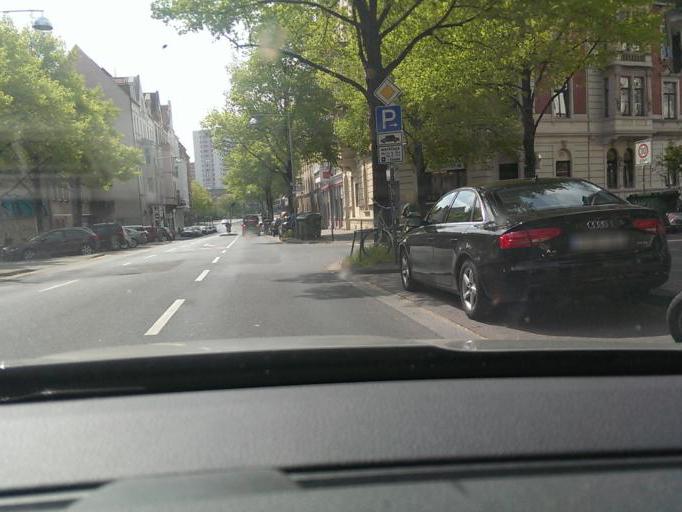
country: DE
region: Lower Saxony
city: Hannover
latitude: 52.3753
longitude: 9.7202
